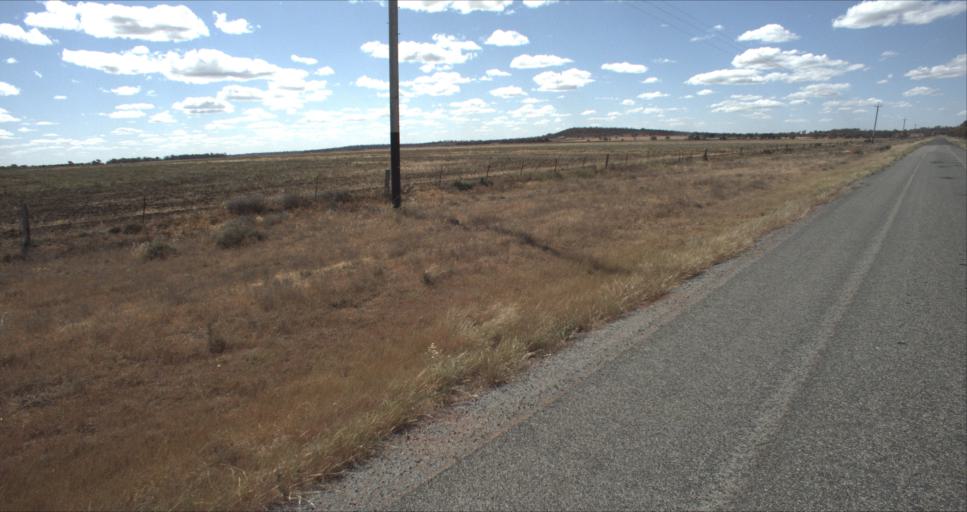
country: AU
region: New South Wales
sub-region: Leeton
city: Leeton
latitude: -34.4404
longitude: 146.2565
